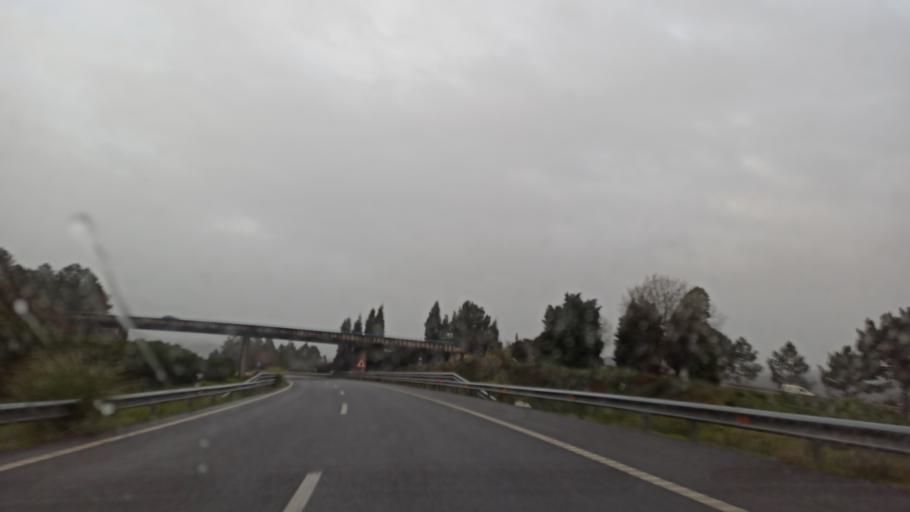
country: ES
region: Galicia
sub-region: Provincia da Coruna
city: Culleredo
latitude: 43.2748
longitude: -8.3680
